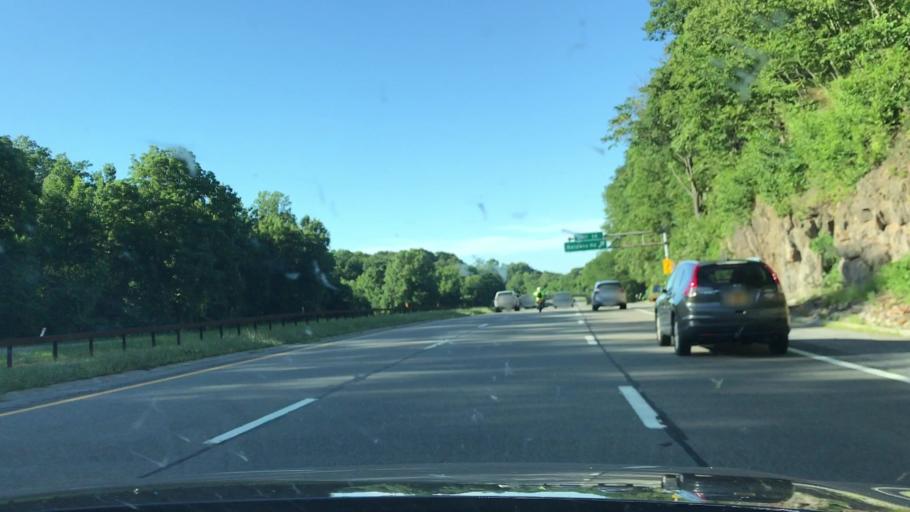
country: US
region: New York
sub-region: Westchester County
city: Yorktown Heights
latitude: 41.2647
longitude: -73.8085
